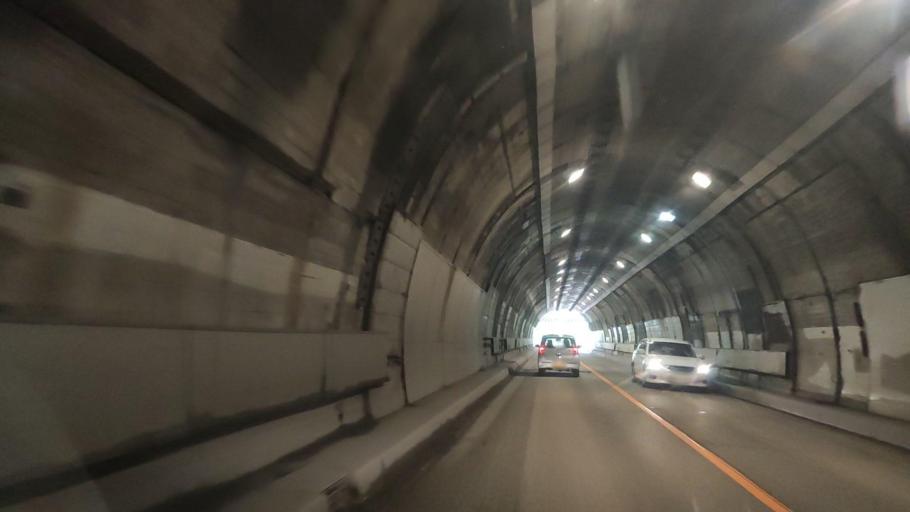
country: JP
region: Hokkaido
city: Date
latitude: 42.5715
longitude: 140.7329
